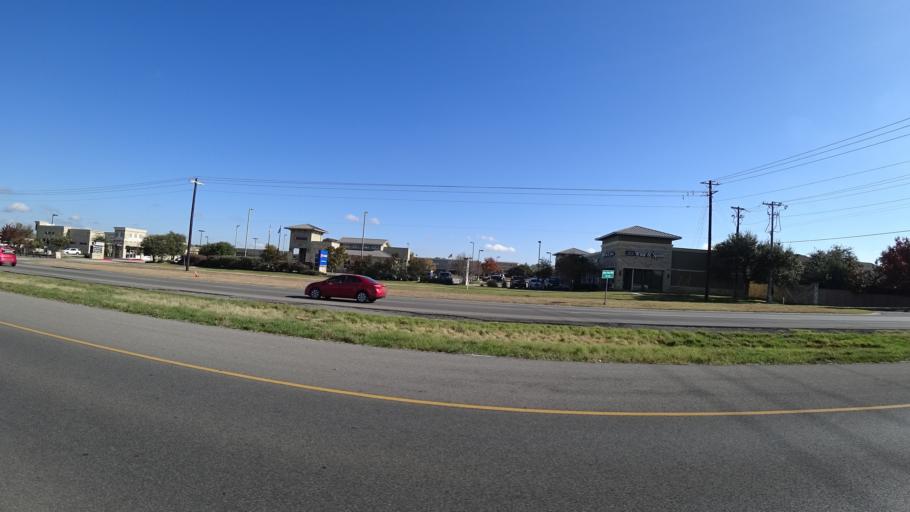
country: US
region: Texas
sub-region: Williamson County
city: Brushy Creek
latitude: 30.4965
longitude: -97.7750
